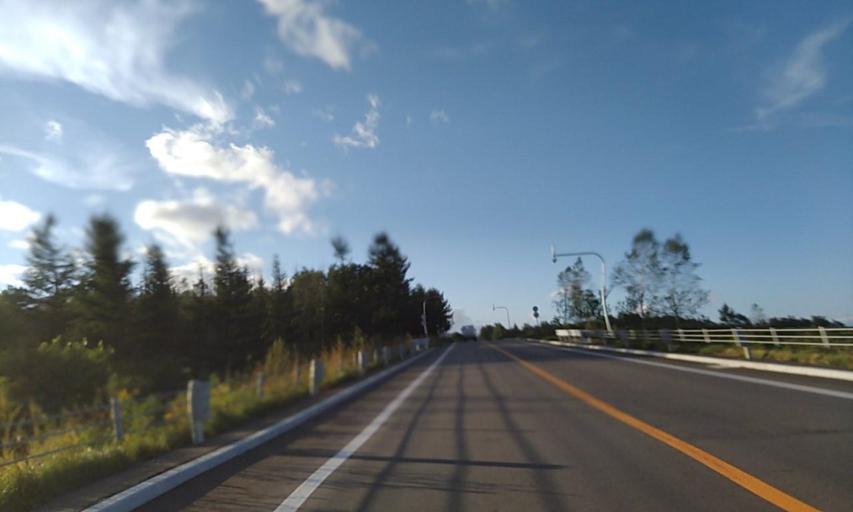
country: JP
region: Hokkaido
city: Otofuke
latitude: 42.9795
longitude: 142.8642
